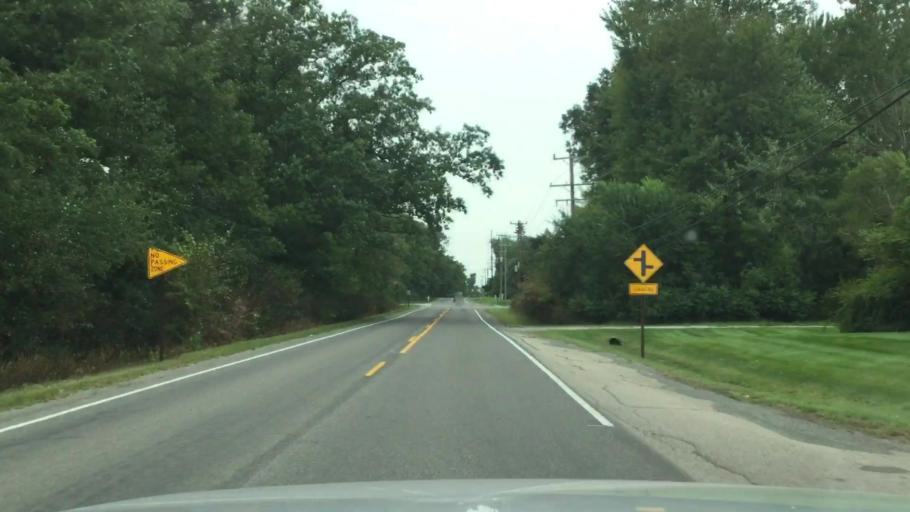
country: US
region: Michigan
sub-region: Washtenaw County
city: Ypsilanti
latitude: 42.2013
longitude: -83.6679
